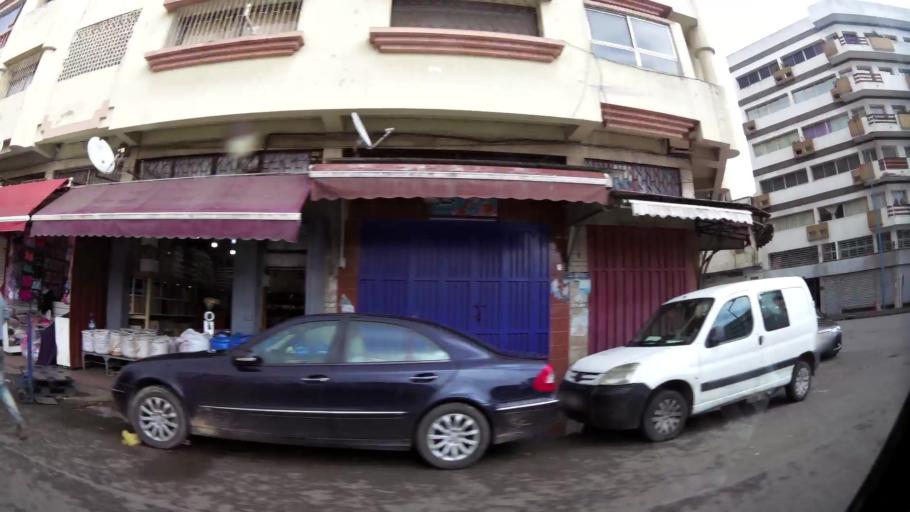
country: MA
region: Grand Casablanca
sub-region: Casablanca
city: Casablanca
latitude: 33.5772
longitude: -7.5984
